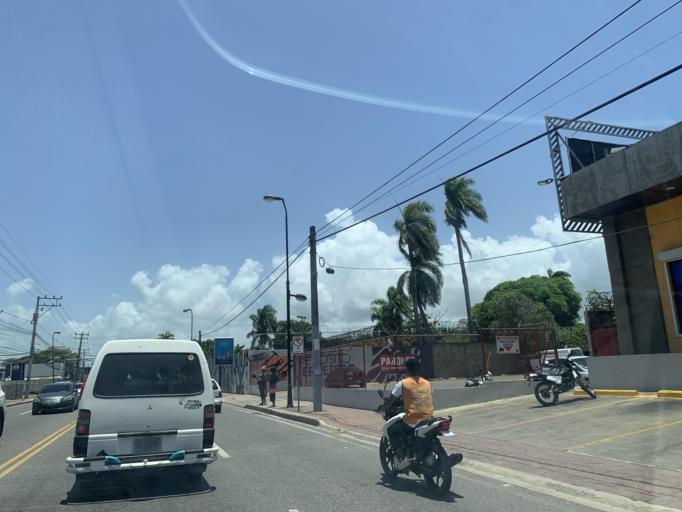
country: DO
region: Puerto Plata
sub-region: Puerto Plata
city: Puerto Plata
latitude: 19.7804
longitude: -70.6710
